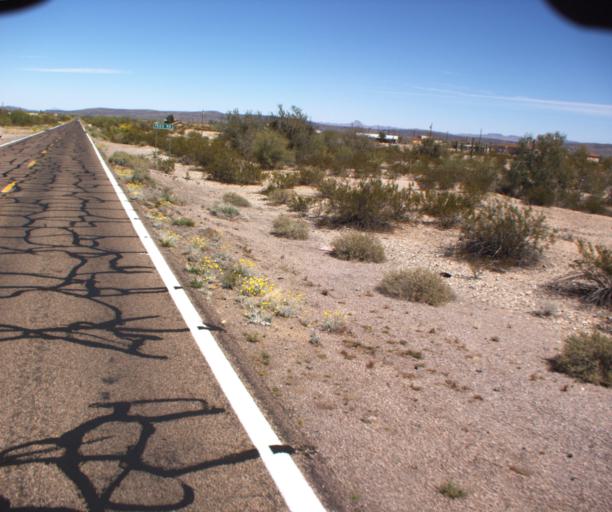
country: US
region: Arizona
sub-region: Pima County
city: Ajo
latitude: 32.4134
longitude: -112.8717
